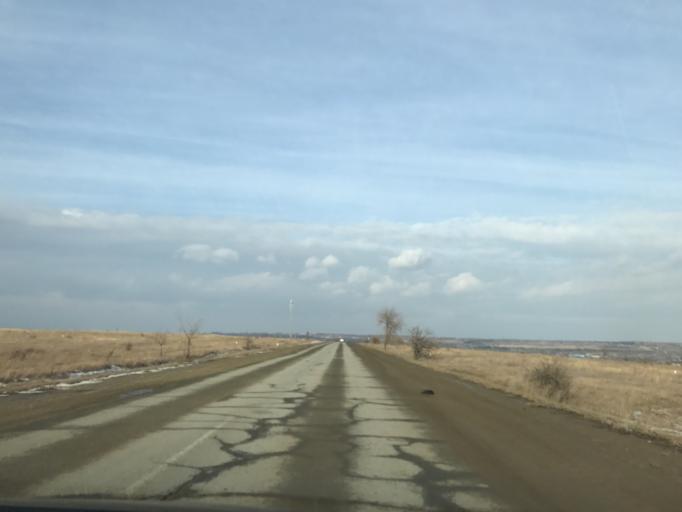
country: RU
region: Rostov
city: Staraya Stanitsa
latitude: 48.2782
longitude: 40.3451
